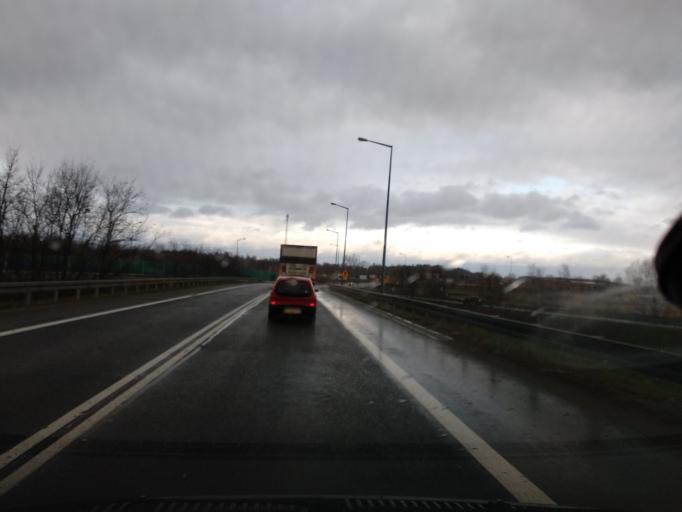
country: PL
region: Greater Poland Voivodeship
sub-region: Powiat koninski
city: Stare Miasto
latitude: 52.1641
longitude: 18.2071
